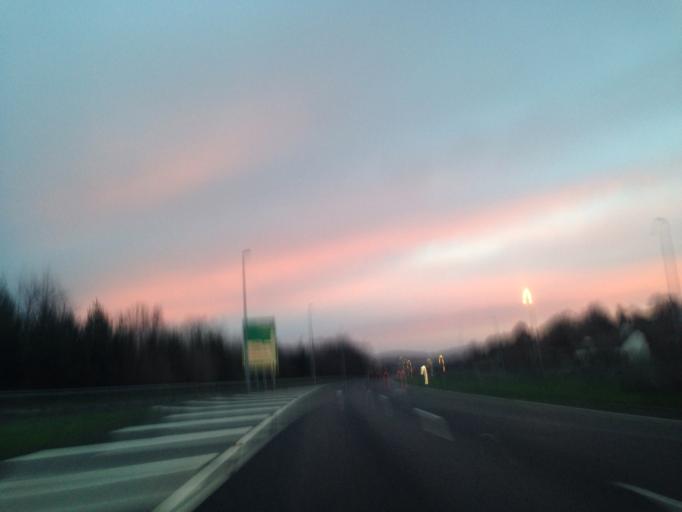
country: IE
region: Leinster
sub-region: Wicklow
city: Kilmacanoge
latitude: 53.1607
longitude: -6.1300
